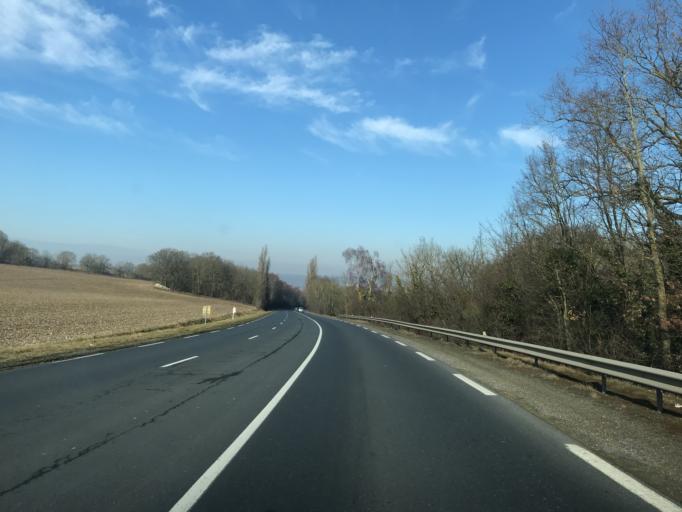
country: FR
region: Haute-Normandie
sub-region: Departement de l'Eure
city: Saint-Pierre-du-Vauvray
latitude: 49.2297
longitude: 1.2103
